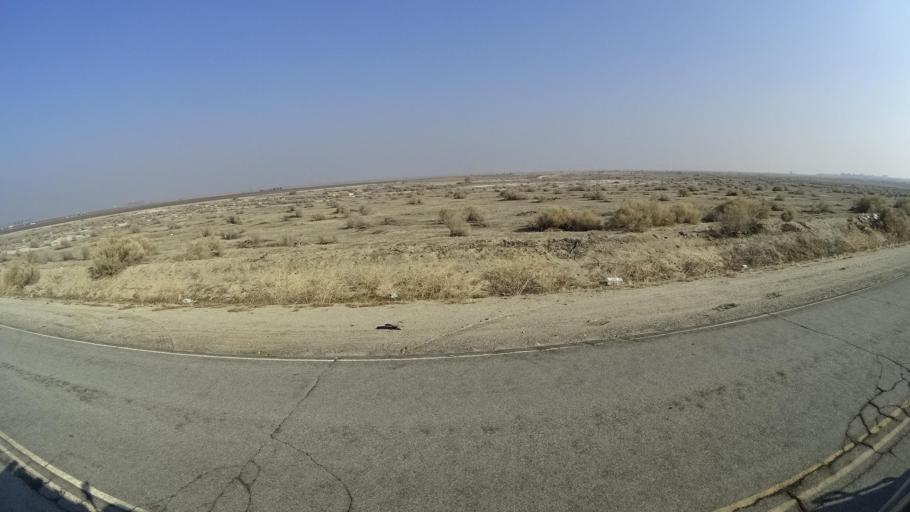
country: US
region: California
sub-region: Kern County
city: Buttonwillow
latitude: 35.3110
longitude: -119.3764
